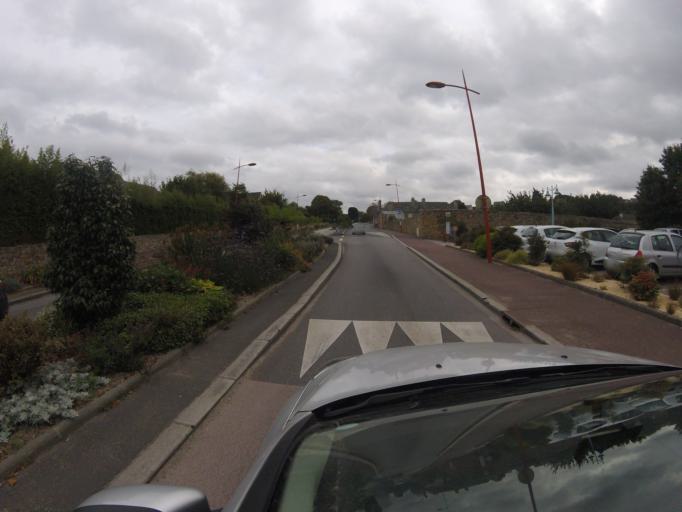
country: FR
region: Lower Normandy
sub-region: Departement de la Manche
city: La Glacerie
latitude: 49.6142
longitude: -1.6034
